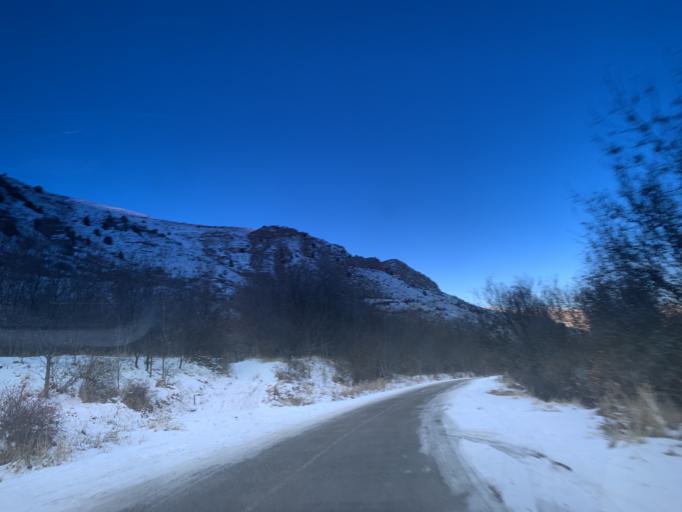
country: AM
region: Vayots' Dzori Marz
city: Areni
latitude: 39.6823
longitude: 45.2319
